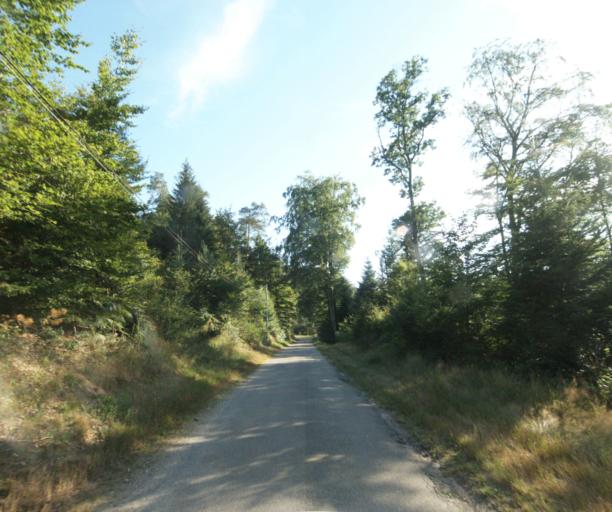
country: FR
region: Lorraine
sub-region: Departement des Vosges
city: Chantraine
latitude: 48.1431
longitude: 6.4327
